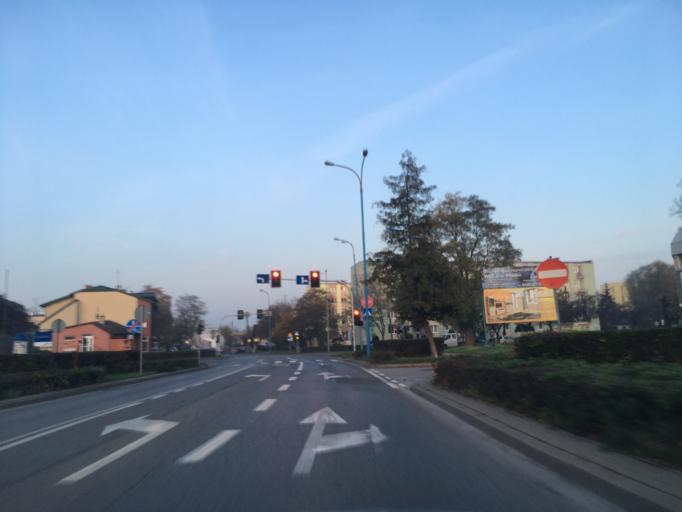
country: PL
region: Lodz Voivodeship
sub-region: Skierniewice
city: Skierniewice
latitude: 51.9557
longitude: 20.1528
